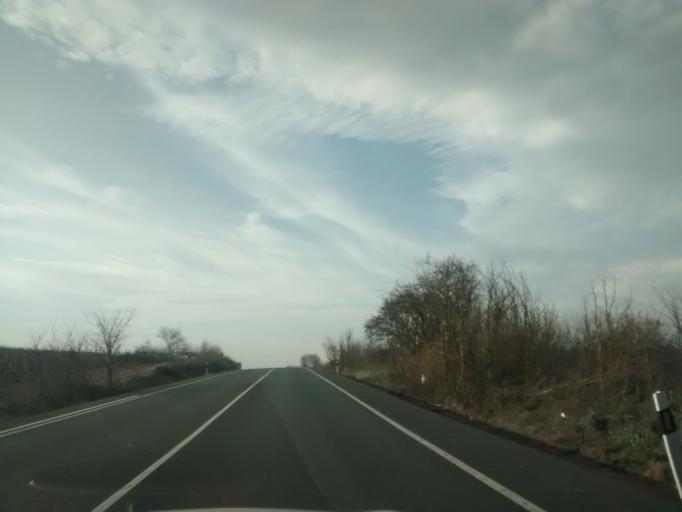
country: ES
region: La Rioja
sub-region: Provincia de La Rioja
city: Torremontalbo
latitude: 42.5073
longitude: -2.6984
